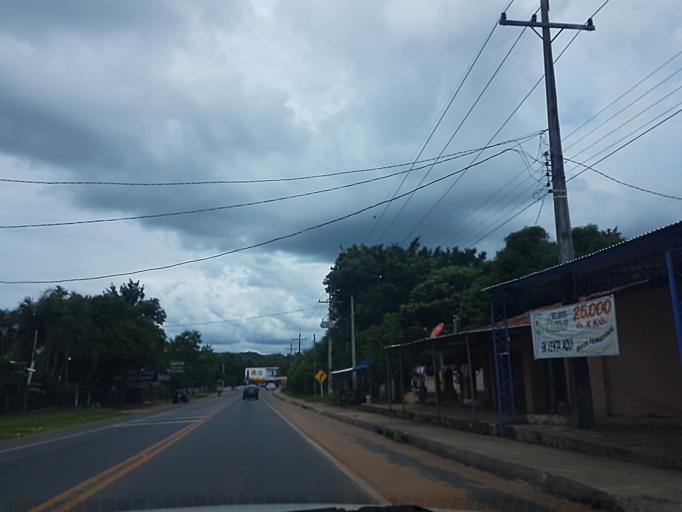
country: PY
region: Central
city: Limpio
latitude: -25.2360
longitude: -57.4435
